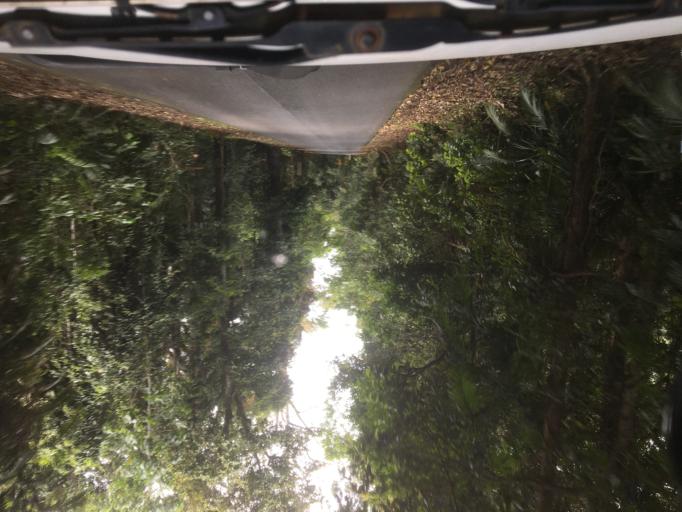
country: AU
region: Queensland
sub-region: Tablelands
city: Tolga
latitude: -17.2787
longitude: 145.6220
